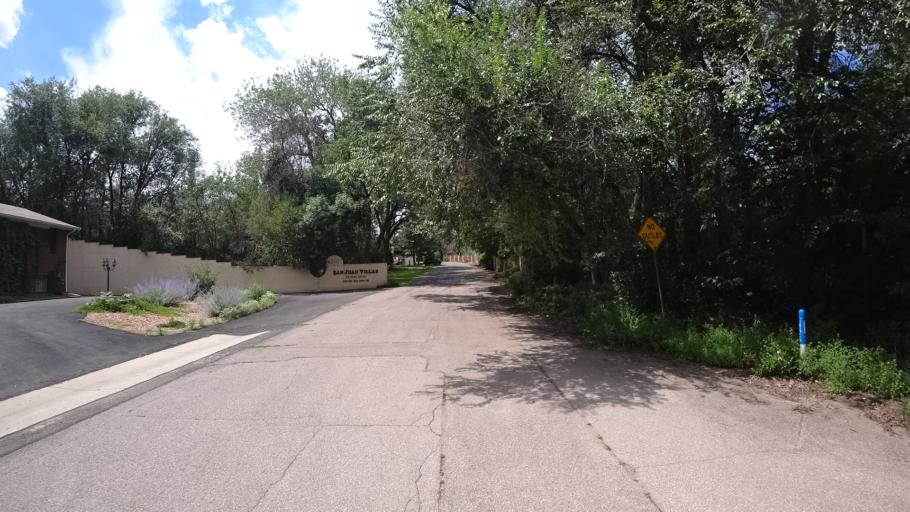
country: US
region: Colorado
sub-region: El Paso County
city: Colorado Springs
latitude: 38.8477
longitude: -104.8370
